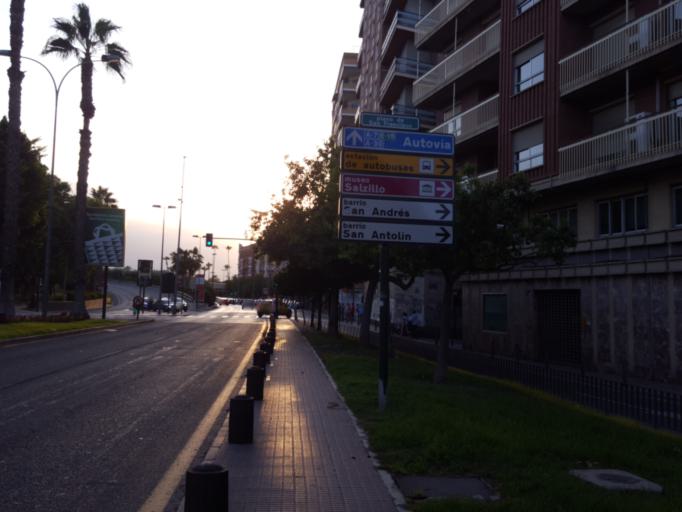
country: ES
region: Murcia
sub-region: Murcia
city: Murcia
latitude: 37.9832
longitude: -1.1362
